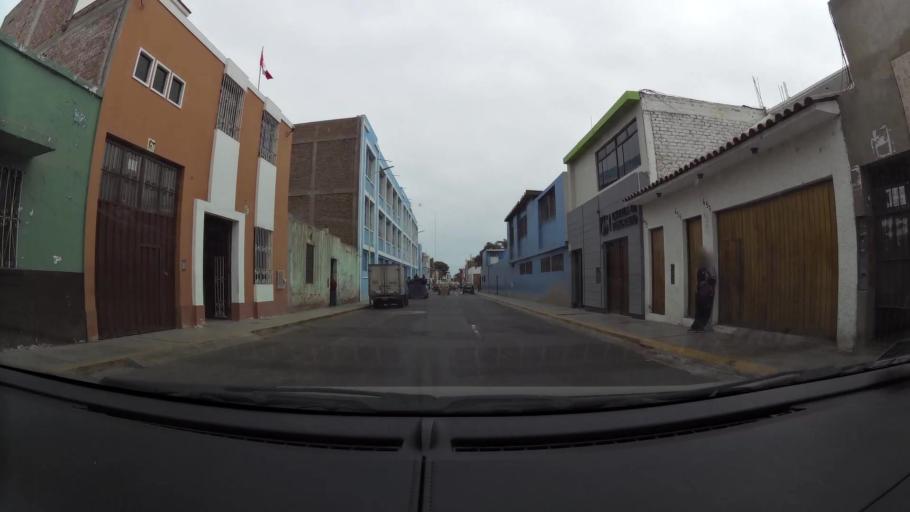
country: PE
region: La Libertad
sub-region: Provincia de Trujillo
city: Trujillo
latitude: -8.1073
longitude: -79.0287
